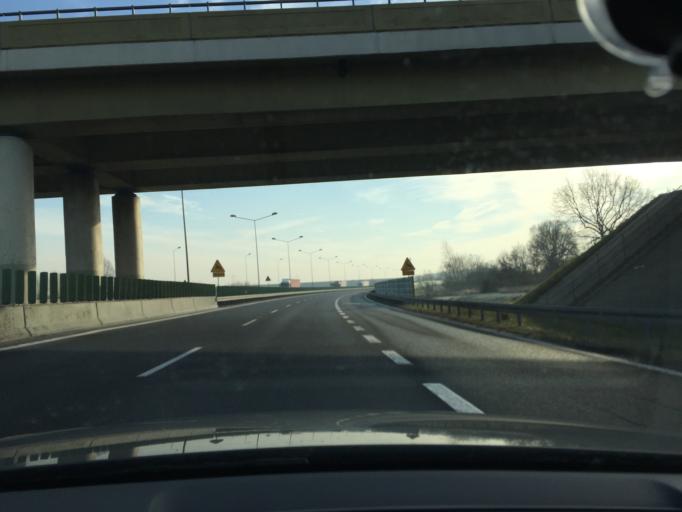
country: PL
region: Silesian Voivodeship
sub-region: Powiat gliwicki
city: Sosnicowice
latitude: 50.3458
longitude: 18.5406
